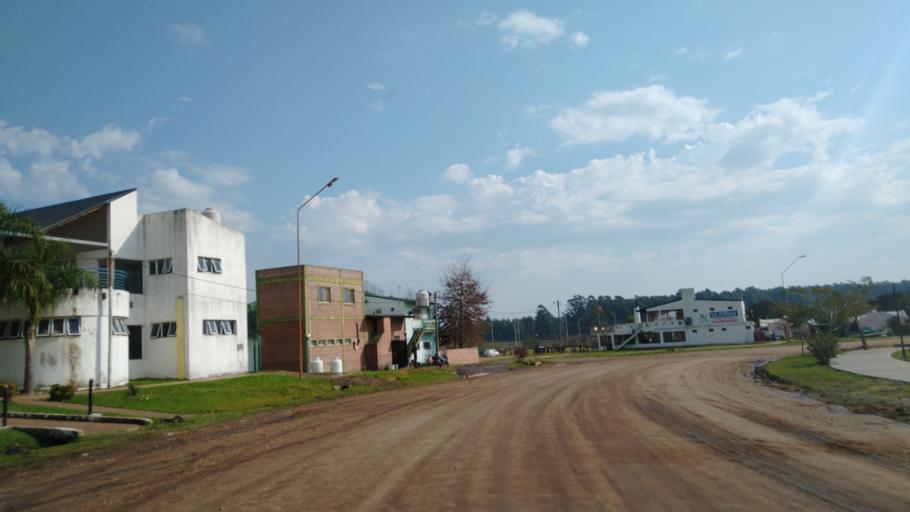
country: AR
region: Entre Rios
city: Chajari
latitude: -30.7439
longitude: -58.0125
